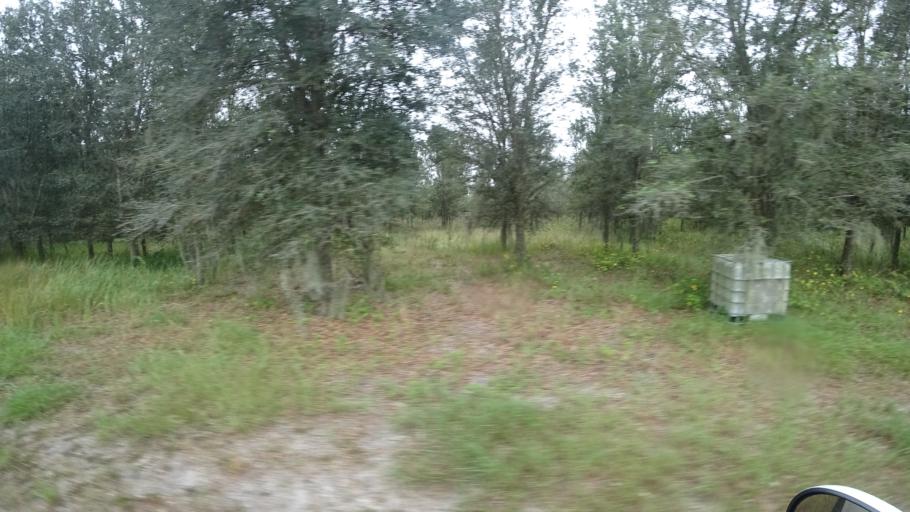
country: US
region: Florida
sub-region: Sarasota County
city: Warm Mineral Springs
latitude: 27.2813
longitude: -82.1746
